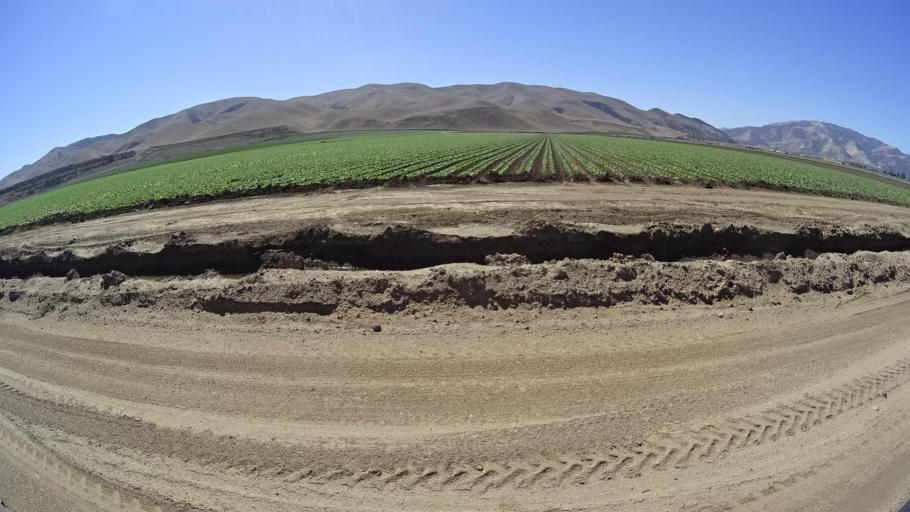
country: US
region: California
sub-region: Monterey County
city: Greenfield
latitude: 36.2927
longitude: -121.2543
